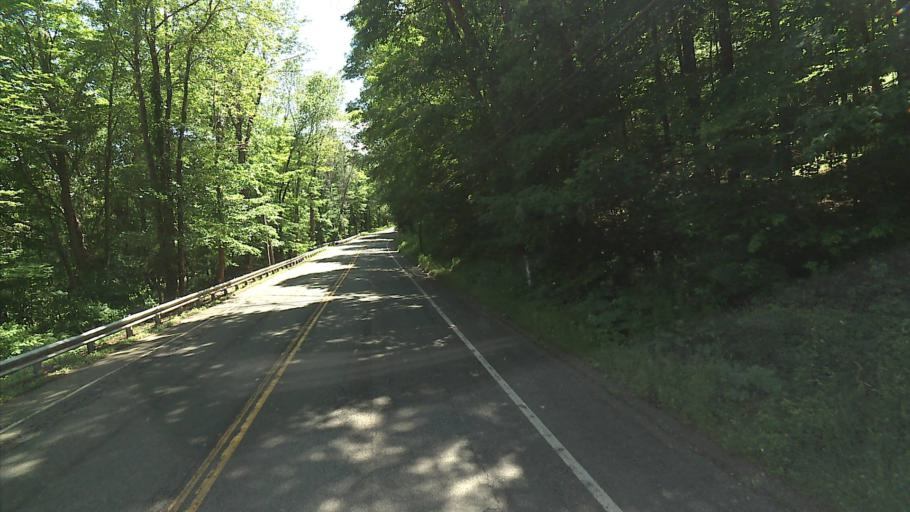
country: US
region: Connecticut
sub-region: New Haven County
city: Woodbridge
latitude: 41.3857
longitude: -72.9999
